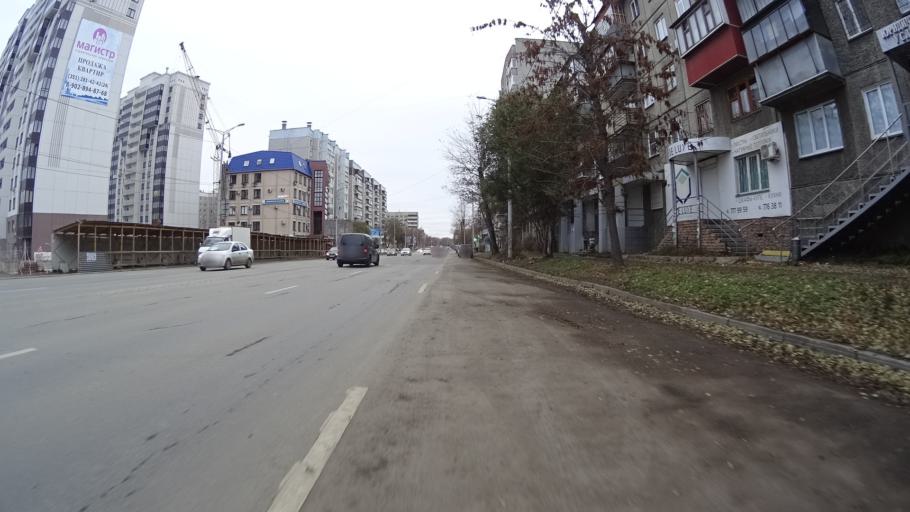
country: RU
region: Chelyabinsk
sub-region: Gorod Chelyabinsk
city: Chelyabinsk
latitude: 55.1577
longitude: 61.4169
